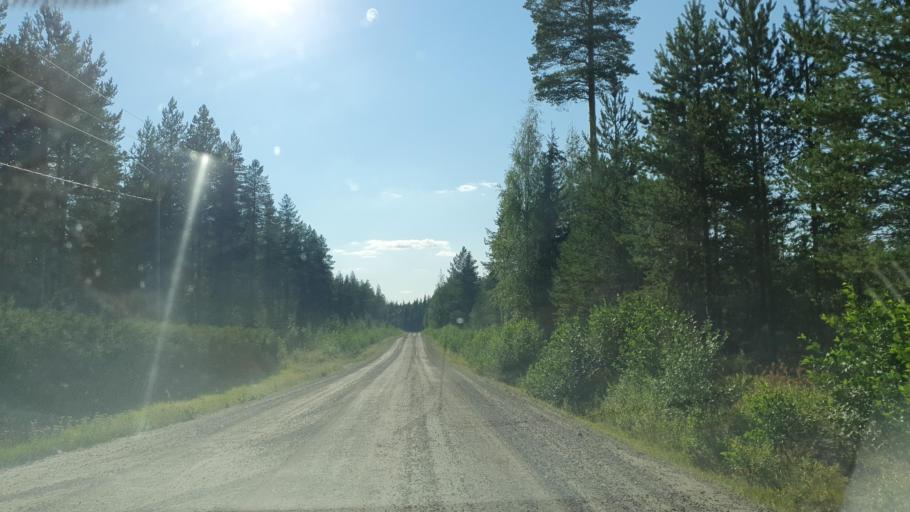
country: FI
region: Kainuu
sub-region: Kehys-Kainuu
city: Kuhmo
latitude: 64.0524
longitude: 29.5777
